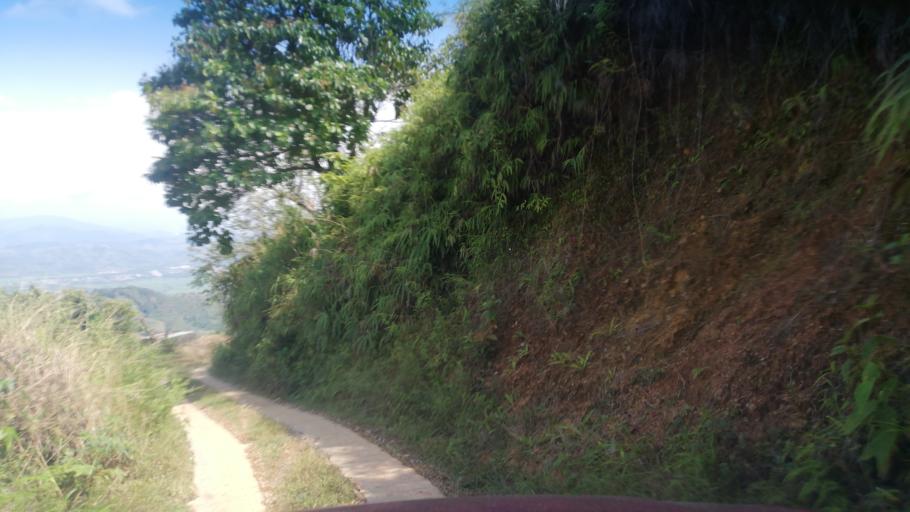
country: CO
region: Risaralda
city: Balboa
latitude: 4.9270
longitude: -75.9595
